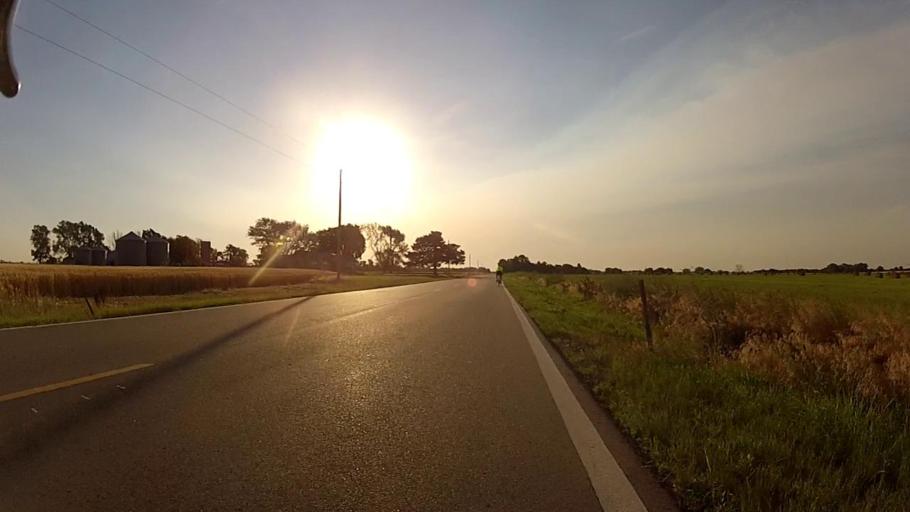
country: US
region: Kansas
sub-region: Harper County
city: Anthony
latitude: 37.1538
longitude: -97.8530
